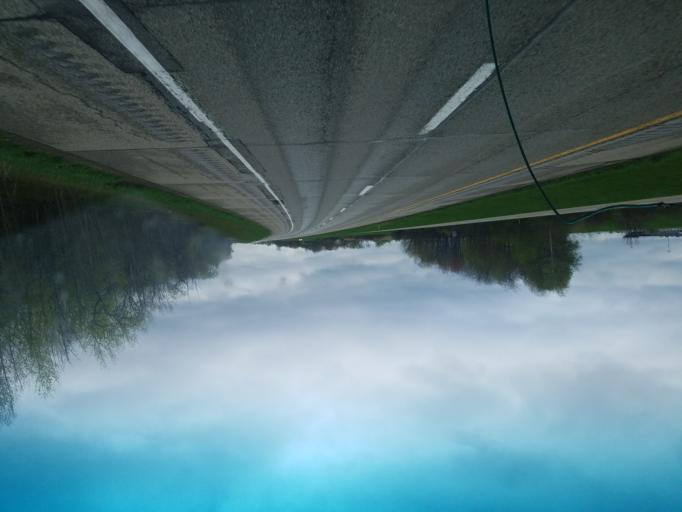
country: US
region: Pennsylvania
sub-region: Erie County
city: North East
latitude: 42.1450
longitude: -79.8368
